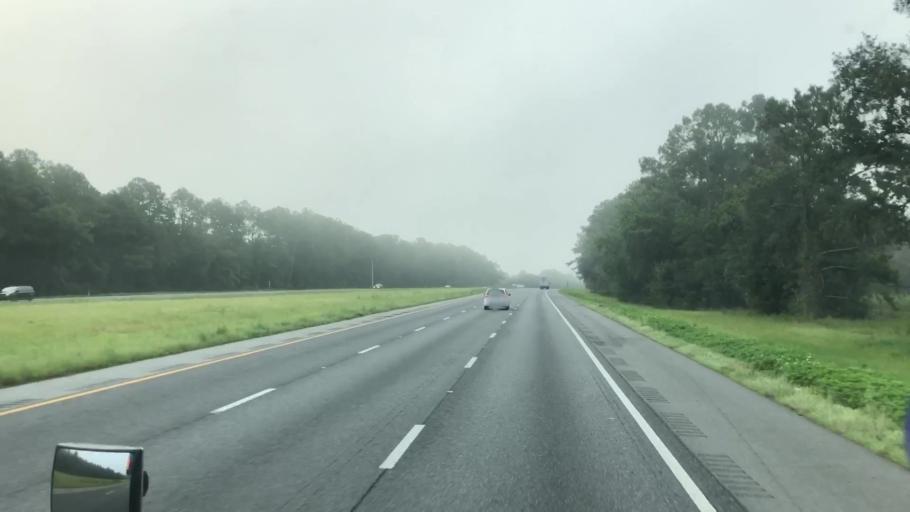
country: US
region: Florida
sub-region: Suwannee County
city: Wellborn
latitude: 30.3588
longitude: -82.8447
